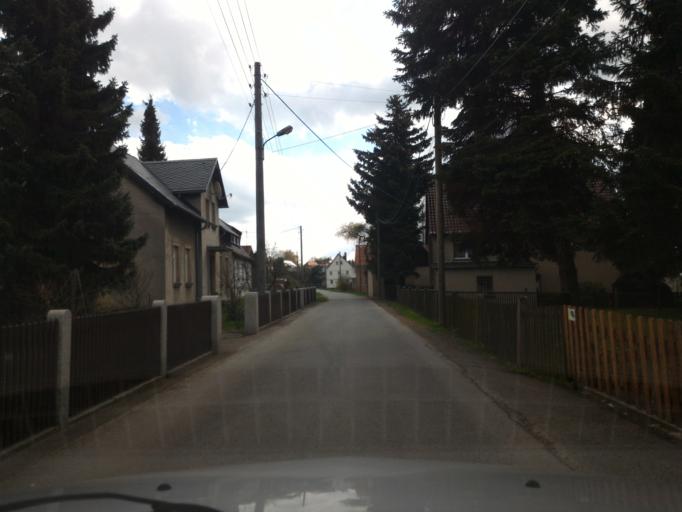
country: DE
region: Saxony
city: Leutersdorf
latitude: 50.9545
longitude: 14.6580
